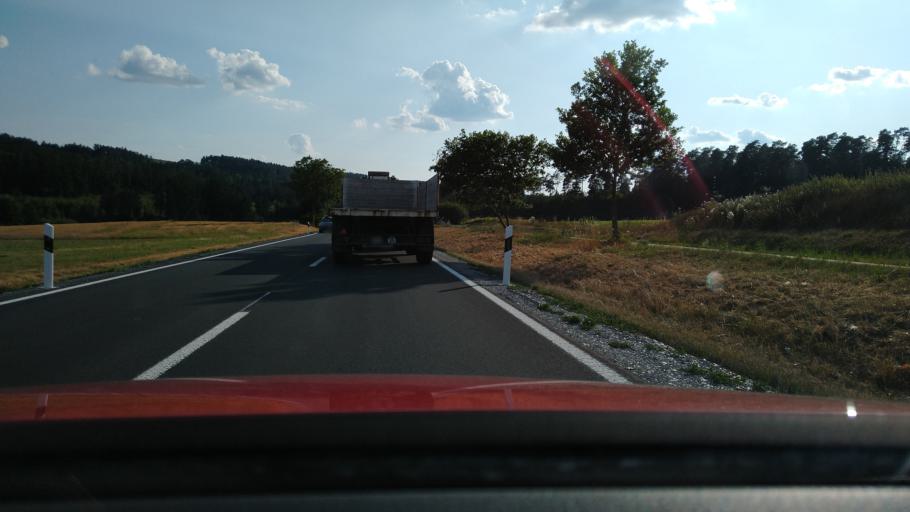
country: DE
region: Bavaria
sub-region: Upper Franconia
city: Mistelgau
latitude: 49.9256
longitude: 11.4410
